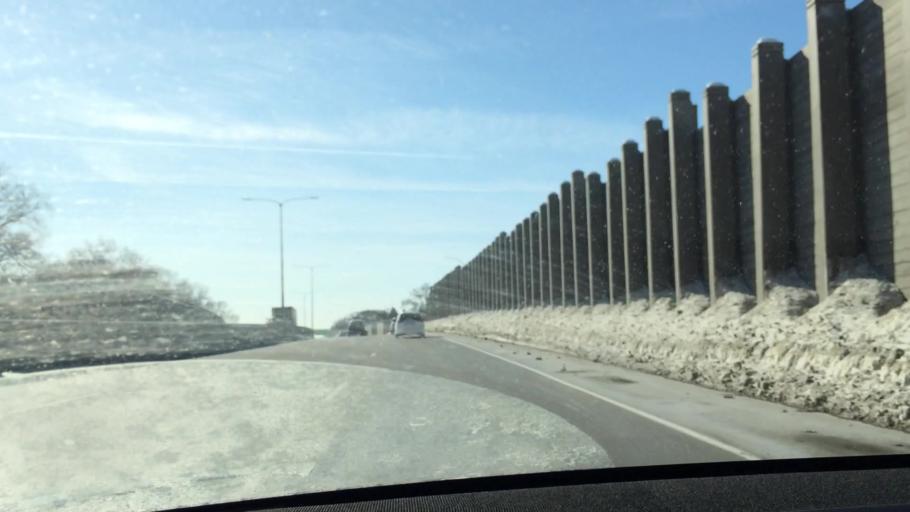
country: US
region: Minnesota
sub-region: Hennepin County
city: Saint Louis Park
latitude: 44.9556
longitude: -93.3479
